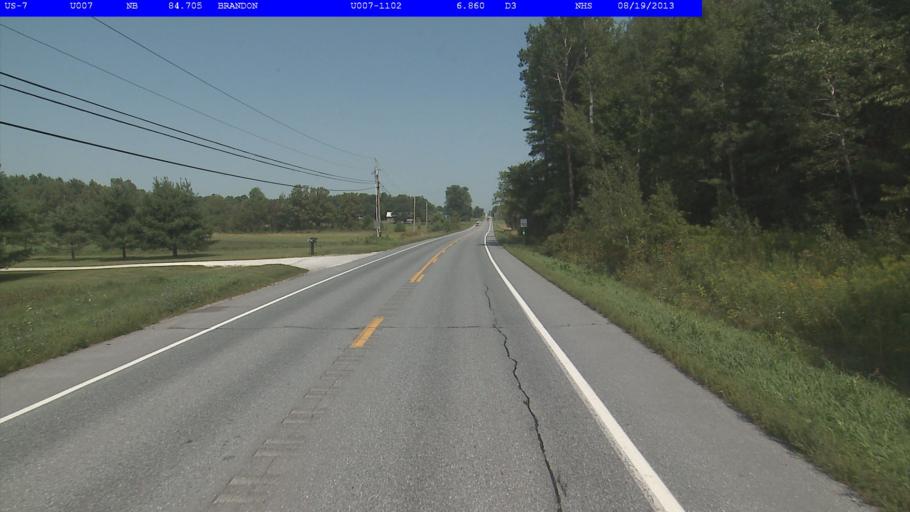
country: US
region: Vermont
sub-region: Rutland County
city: Brandon
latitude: 43.8351
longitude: -73.1060
